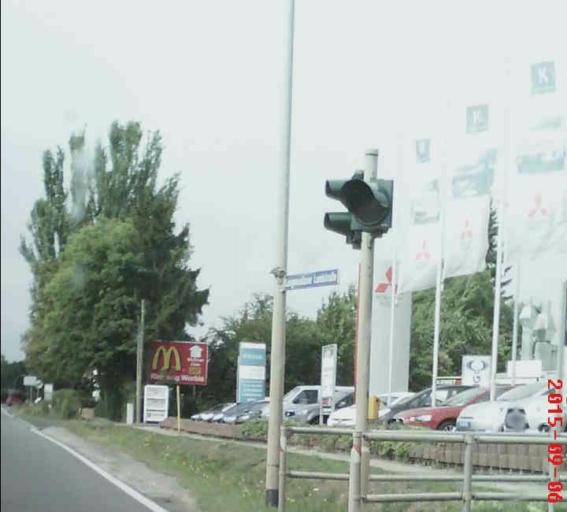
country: DE
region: Thuringia
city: Muehlhausen
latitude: 51.1990
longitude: 10.4782
